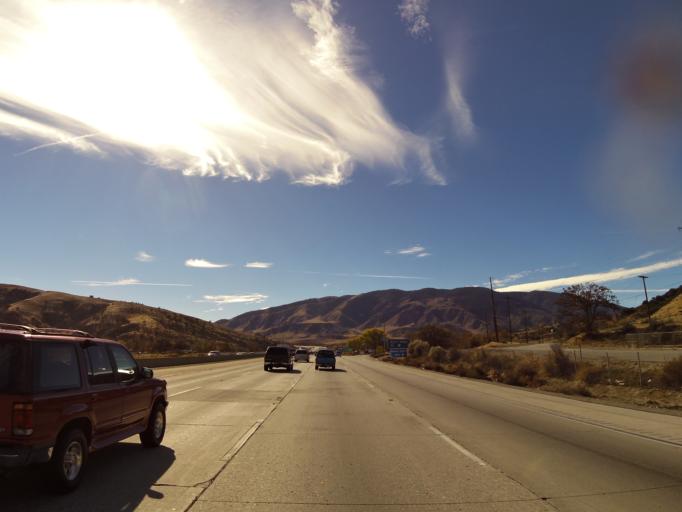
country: US
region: California
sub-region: Kern County
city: Lebec
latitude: 34.8316
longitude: -118.8677
